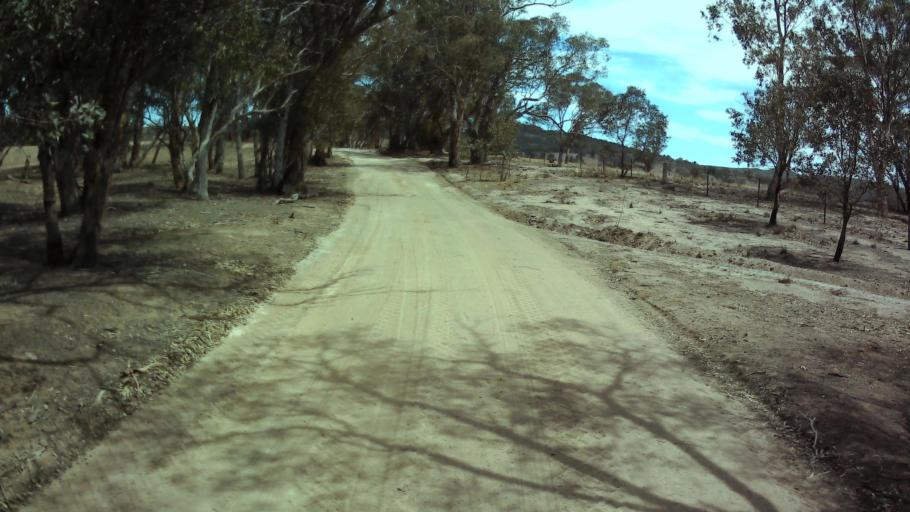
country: AU
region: New South Wales
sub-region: Weddin
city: Grenfell
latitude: -33.7790
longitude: 148.1515
